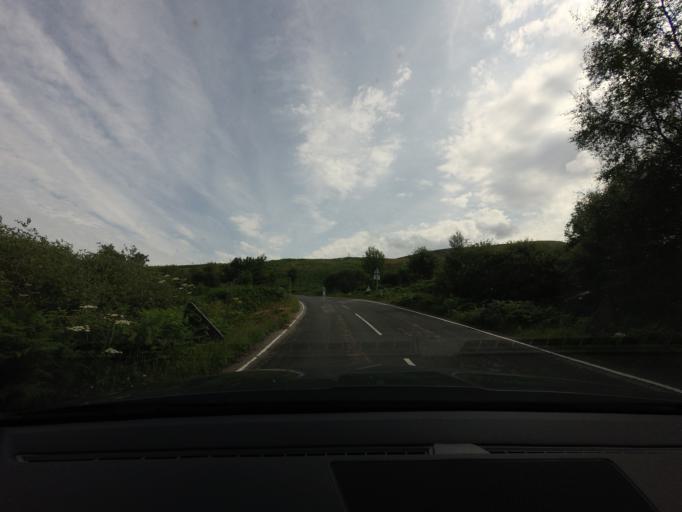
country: GB
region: Scotland
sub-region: Highland
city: Alness
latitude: 57.8437
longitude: -4.2902
